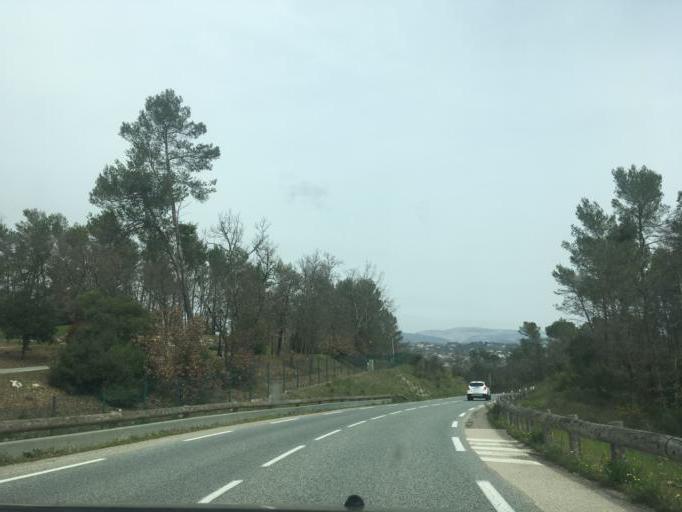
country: FR
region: Provence-Alpes-Cote d'Azur
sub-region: Departement du Var
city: Callian
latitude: 43.5943
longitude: 6.7411
